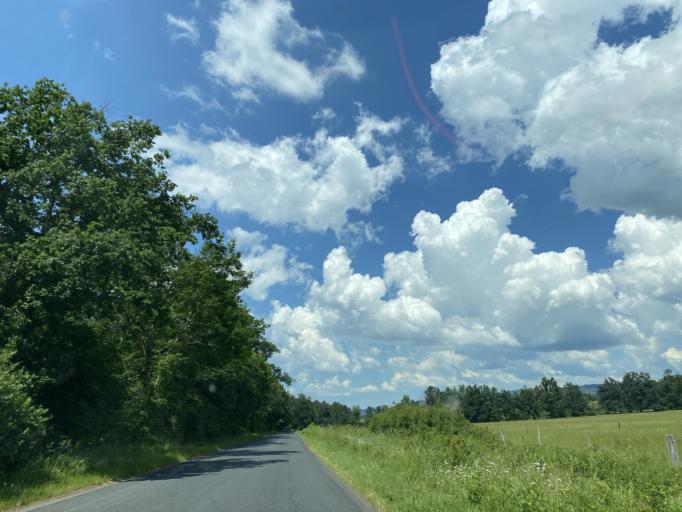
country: FR
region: Auvergne
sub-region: Departement du Puy-de-Dome
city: Courpiere
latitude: 45.7702
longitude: 3.5505
